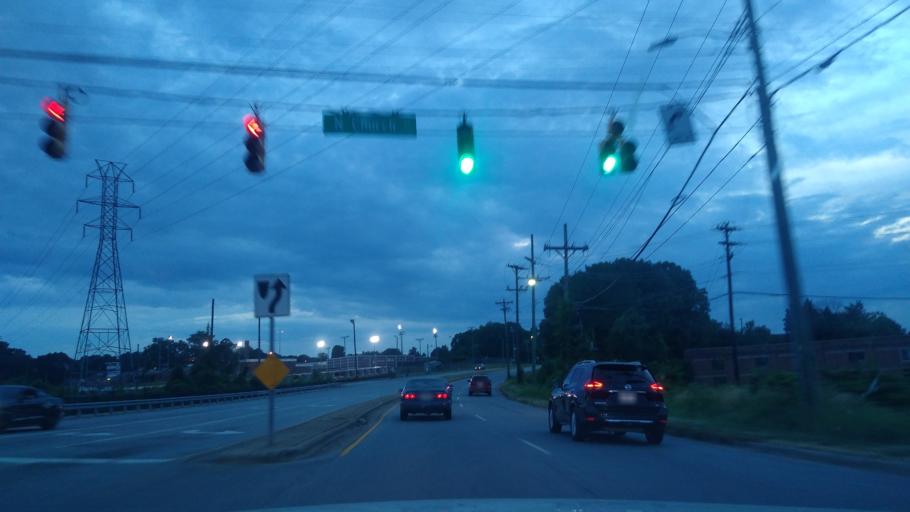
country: US
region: North Carolina
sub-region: Guilford County
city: Greensboro
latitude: 36.1114
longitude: -79.7811
